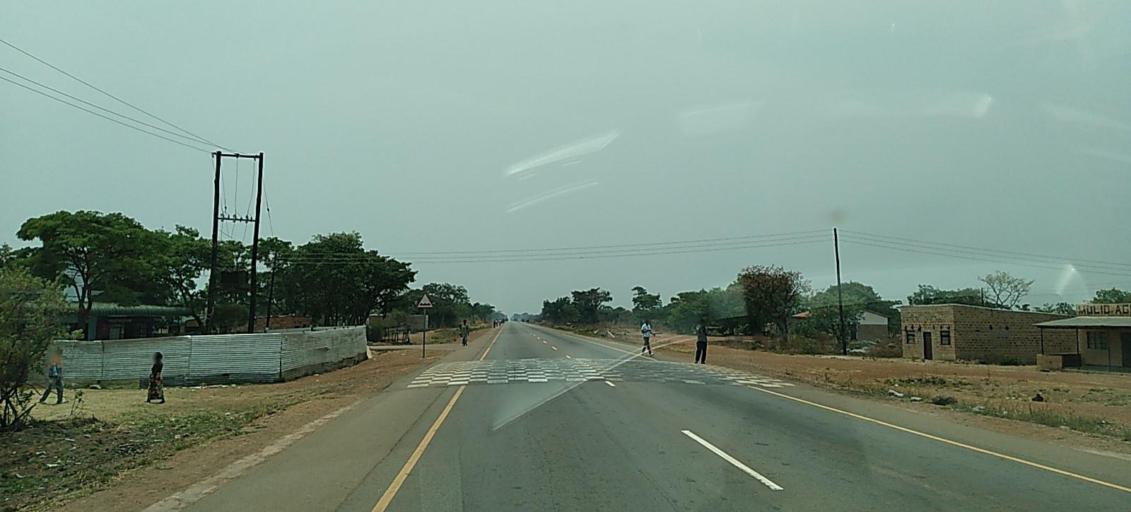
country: CD
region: Katanga
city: Kipushi
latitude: -12.3353
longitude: 27.0668
